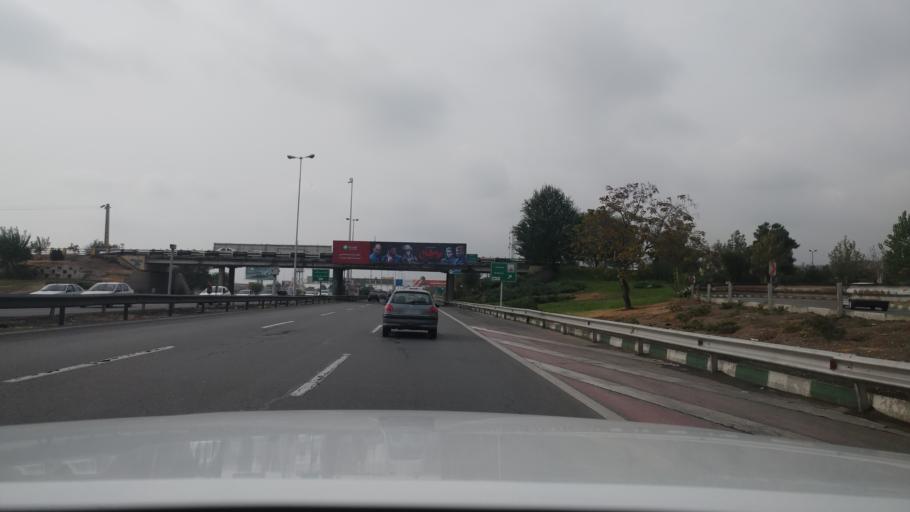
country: IR
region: Tehran
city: Shahr-e Qods
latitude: 35.7159
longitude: 51.2422
